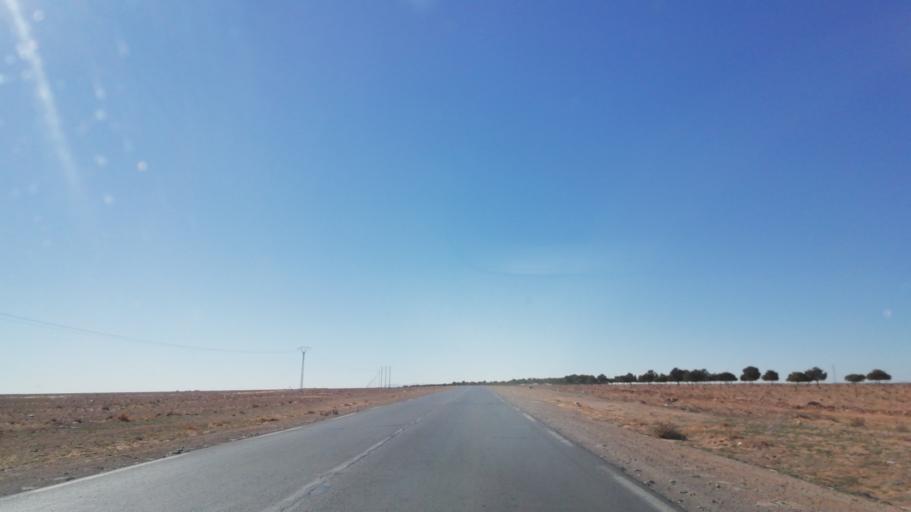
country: DZ
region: Saida
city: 'Ain el Hadjar
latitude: 34.0039
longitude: 0.0464
